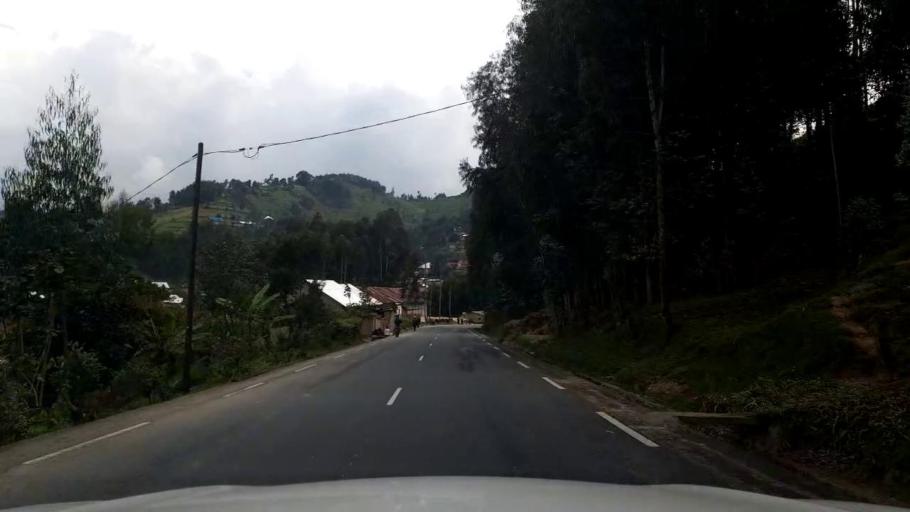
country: RW
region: Northern Province
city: Musanze
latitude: -1.6829
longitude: 29.5164
